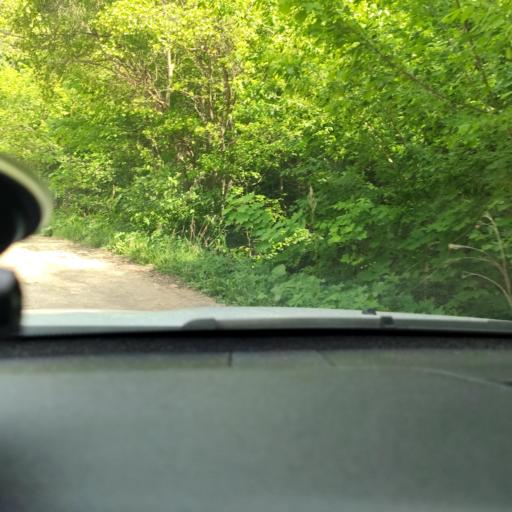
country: RU
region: Samara
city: Volzhskiy
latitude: 53.3371
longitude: 50.2078
